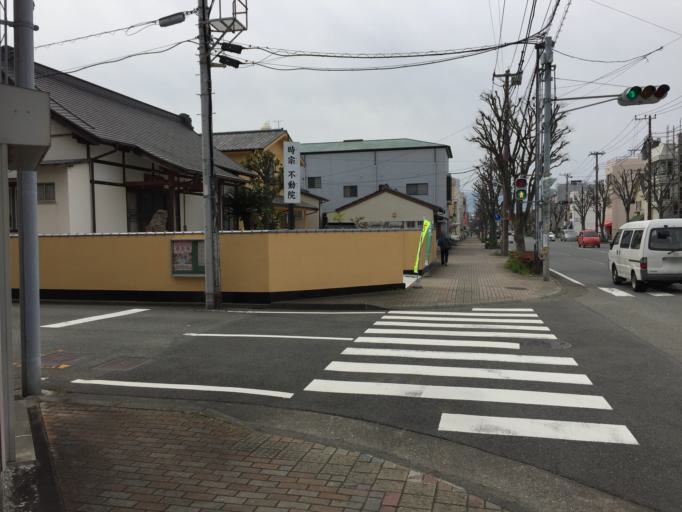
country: JP
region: Shizuoka
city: Numazu
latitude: 35.0928
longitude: 138.8570
